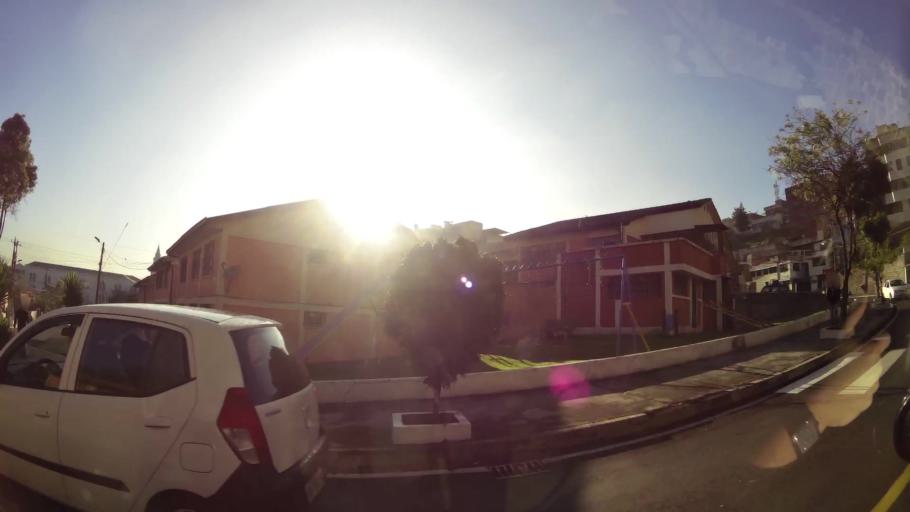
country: EC
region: Pichincha
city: Quito
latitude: -0.2359
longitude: -78.5144
